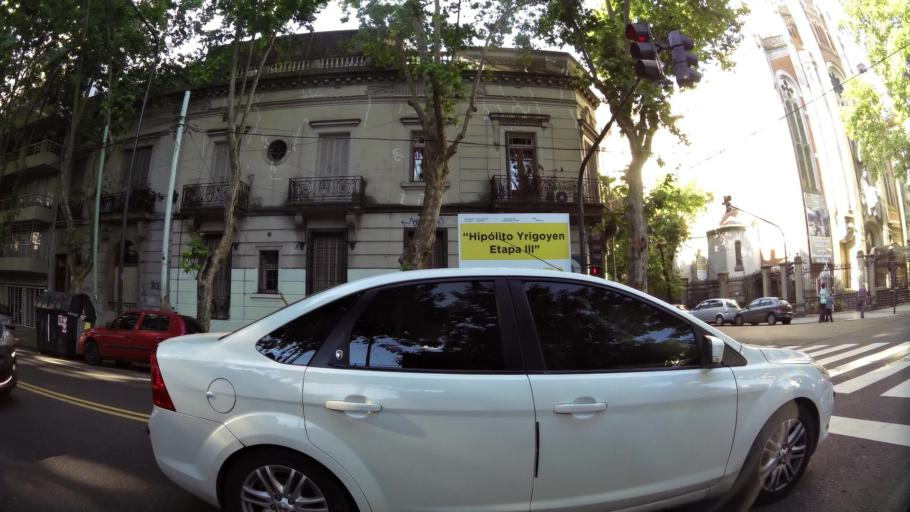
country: AR
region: Buenos Aires F.D.
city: Buenos Aires
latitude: -34.6148
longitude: -58.4231
